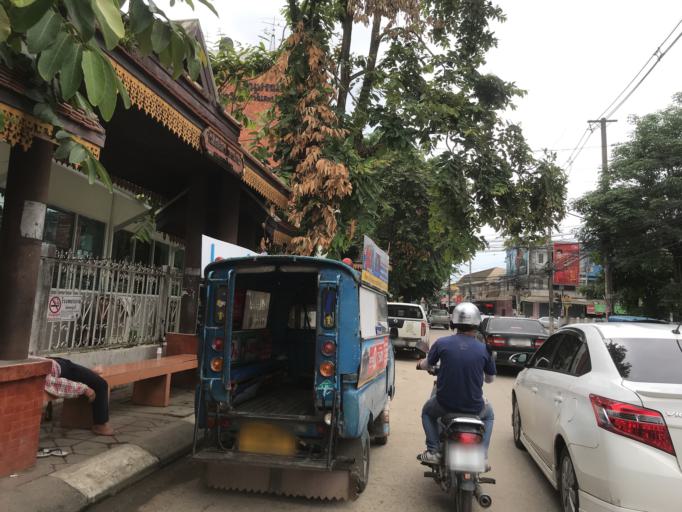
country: TH
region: Chiang Rai
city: Chiang Rai
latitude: 19.9018
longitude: 99.8290
